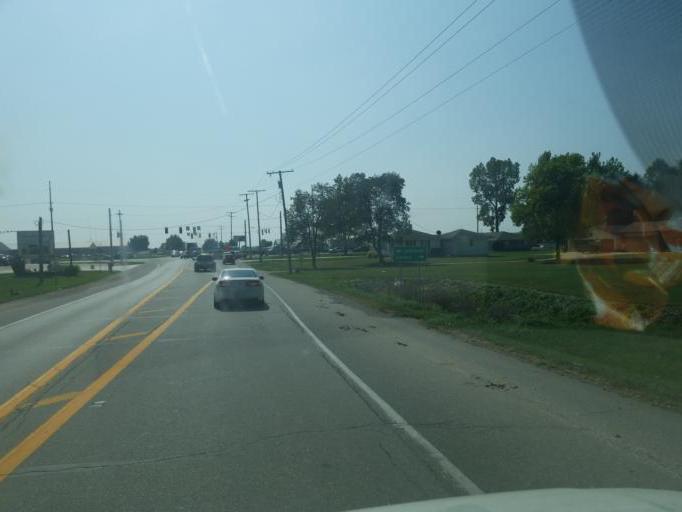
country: US
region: Indiana
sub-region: LaGrange County
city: Topeka
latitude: 41.6558
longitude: -85.5803
